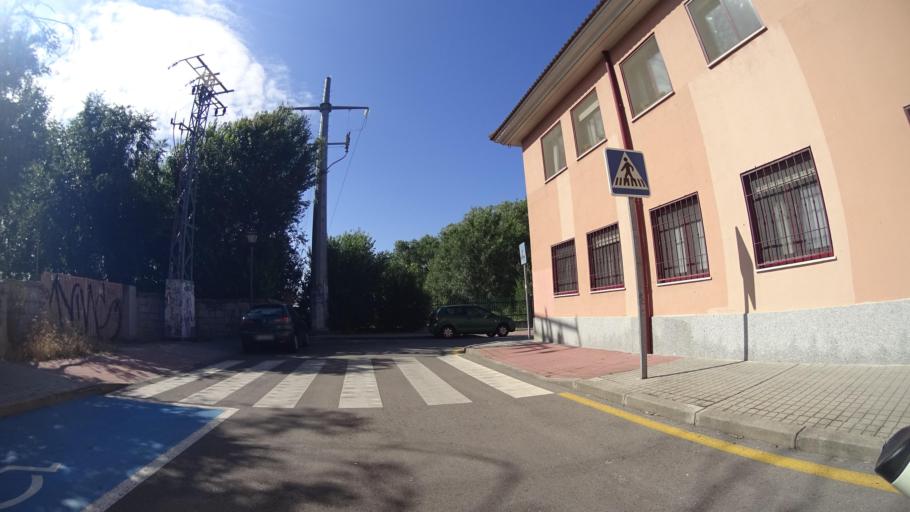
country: ES
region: Madrid
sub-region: Provincia de Madrid
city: Las Matas
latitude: 40.5445
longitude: -3.8913
